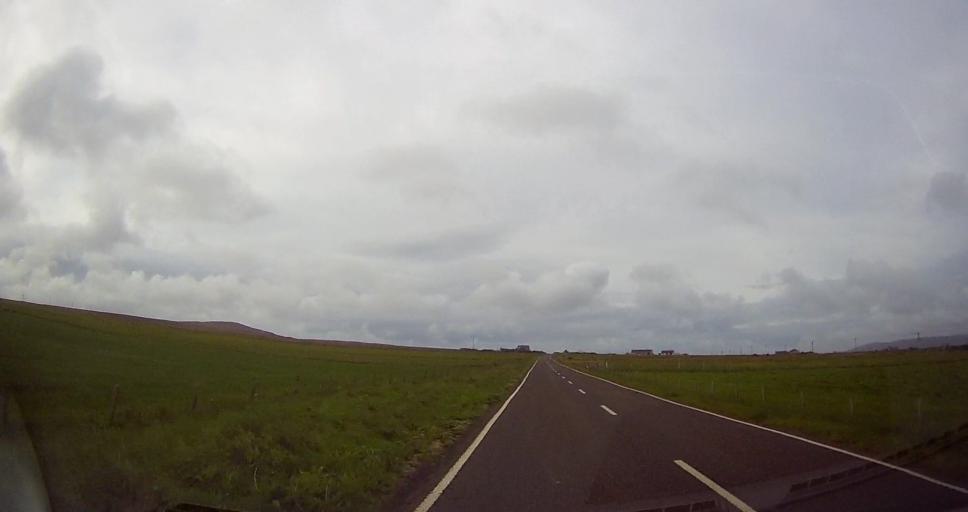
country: GB
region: Scotland
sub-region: Orkney Islands
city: Stromness
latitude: 58.9604
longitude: -3.2223
